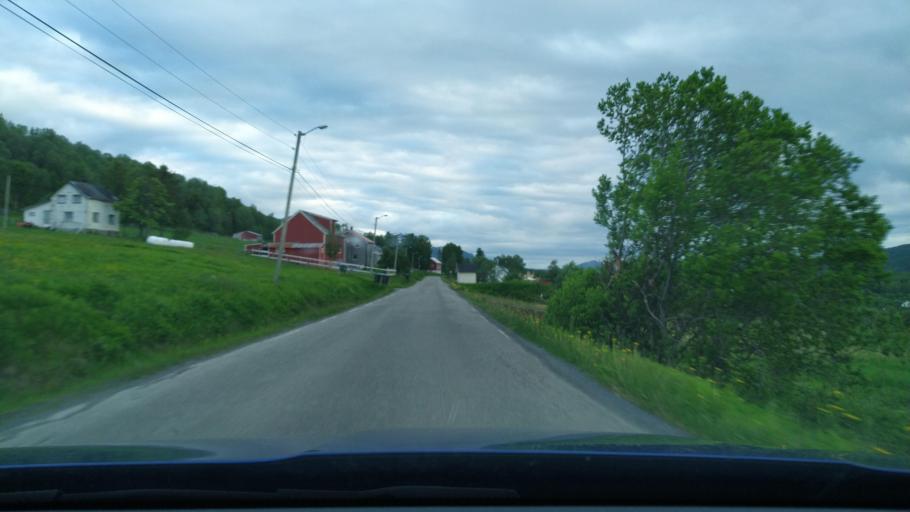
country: NO
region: Troms
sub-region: Tranoy
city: Vangsvika
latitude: 69.1156
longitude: 17.7973
